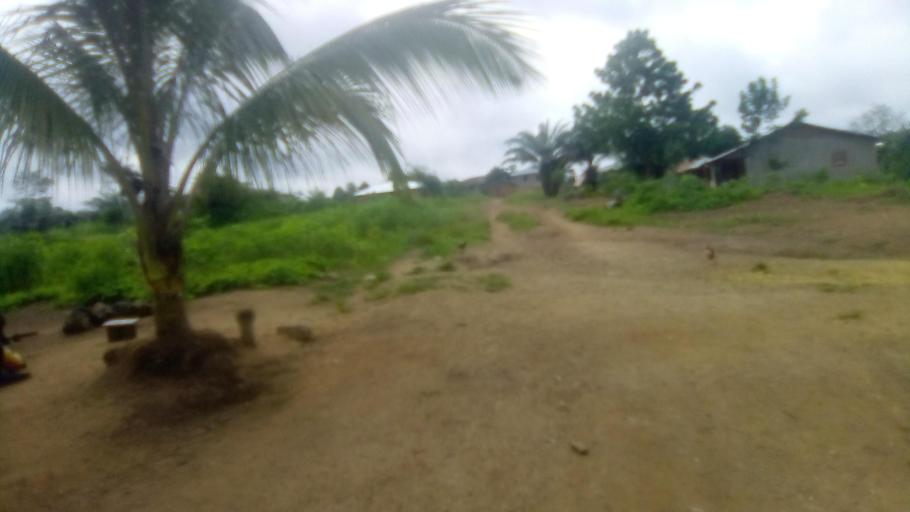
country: SL
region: Eastern Province
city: Kailahun
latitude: 8.2696
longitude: -10.5686
